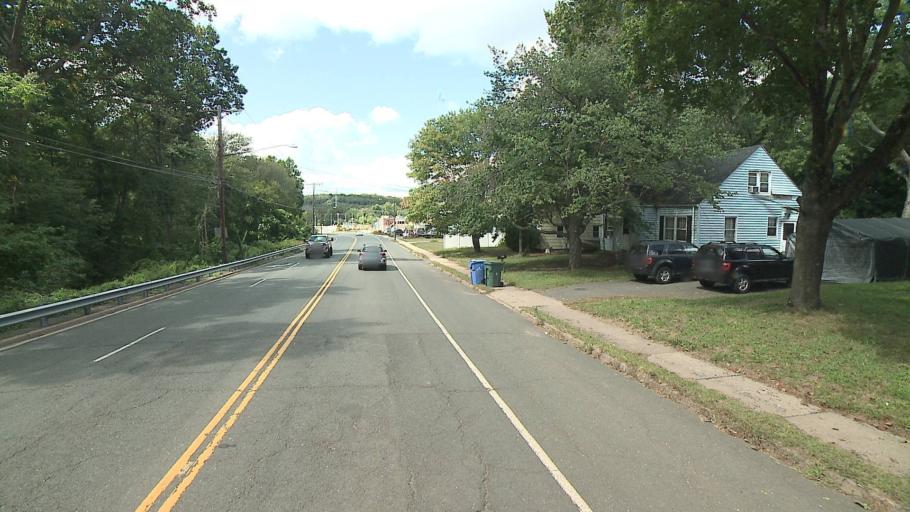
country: US
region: Connecticut
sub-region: Hartford County
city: Manchester
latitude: 41.7798
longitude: -72.5581
